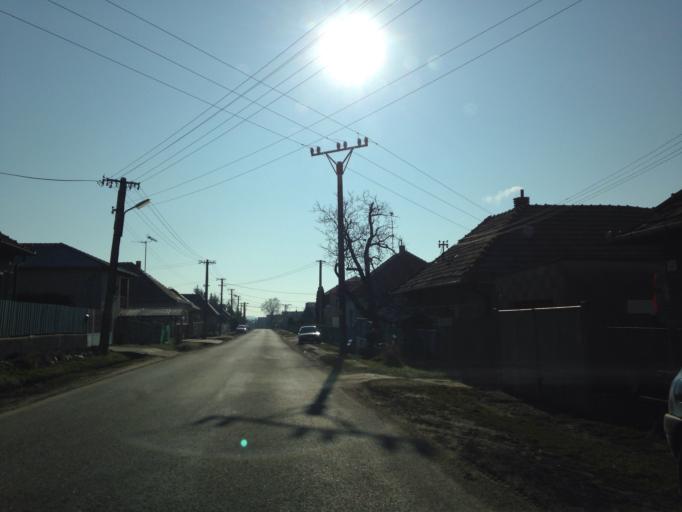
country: SK
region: Nitriansky
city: Svodin
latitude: 47.9080
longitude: 18.4115
